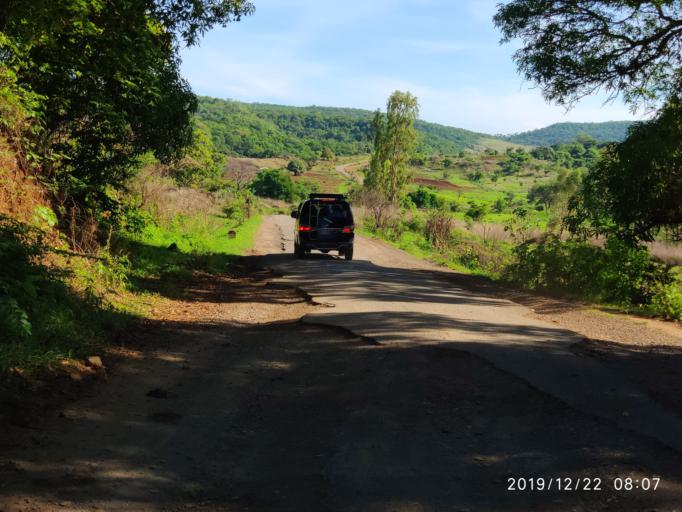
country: MG
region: Diana
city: Ambilobe
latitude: -12.9309
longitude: 49.1614
